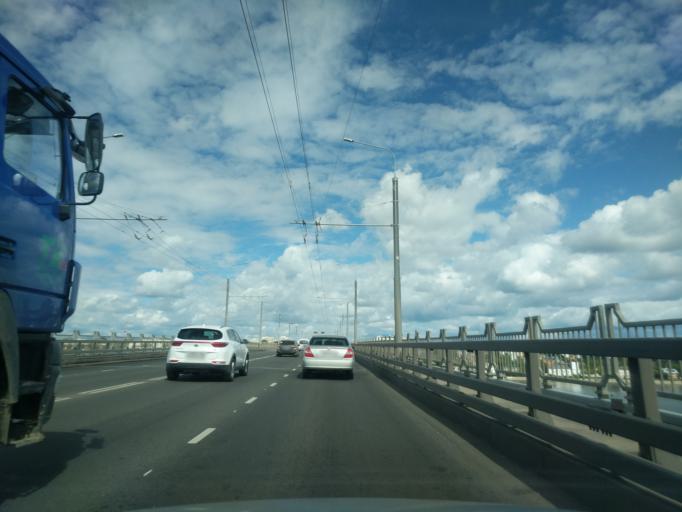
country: RU
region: Kostroma
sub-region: Kostromskoy Rayon
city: Kostroma
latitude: 57.7526
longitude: 40.9377
